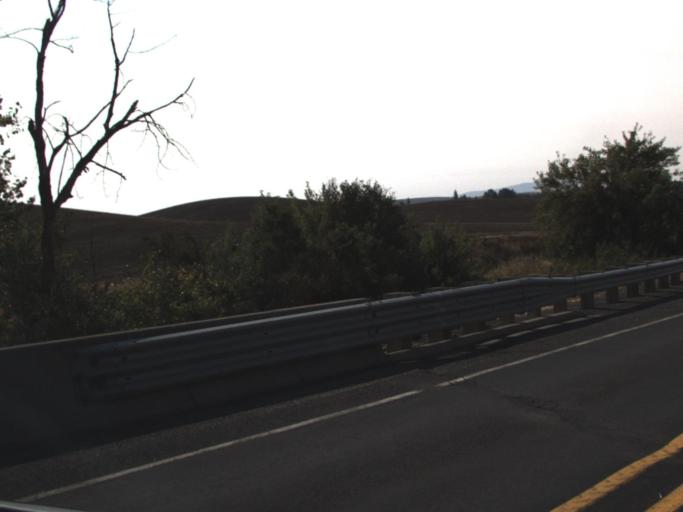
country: US
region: Washington
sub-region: Whitman County
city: Colfax
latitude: 47.0219
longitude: -117.1470
